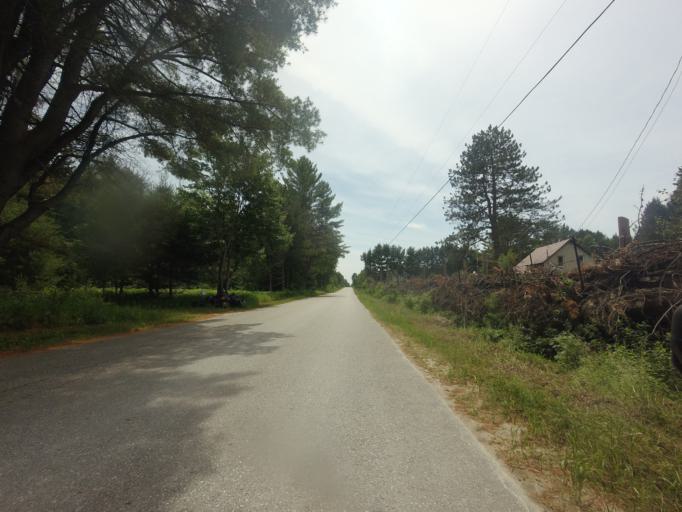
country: CA
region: Quebec
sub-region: Outaouais
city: Wakefield
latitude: 45.9570
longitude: -76.0605
